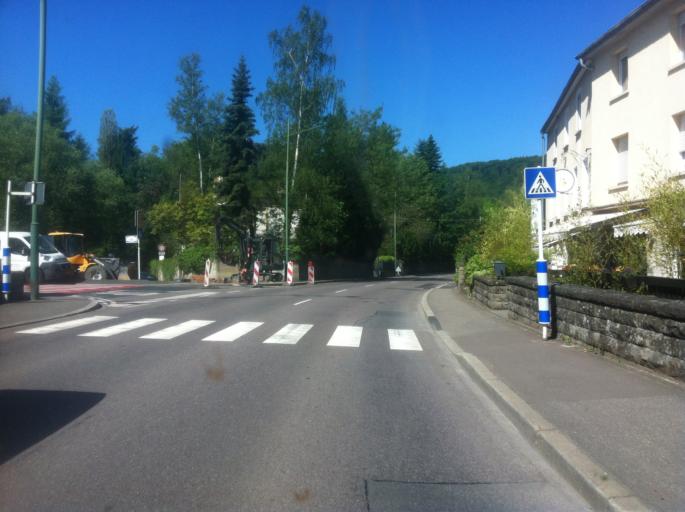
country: LU
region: Grevenmacher
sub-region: Canton d'Echternach
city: Echternach
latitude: 49.8100
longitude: 6.4231
